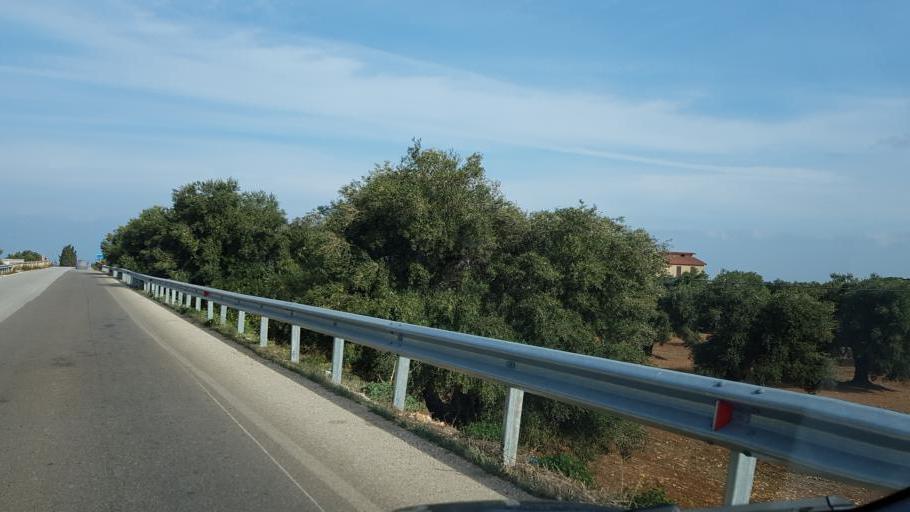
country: IT
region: Apulia
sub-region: Provincia di Brindisi
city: Ostuni
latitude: 40.7505
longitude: 17.5823
